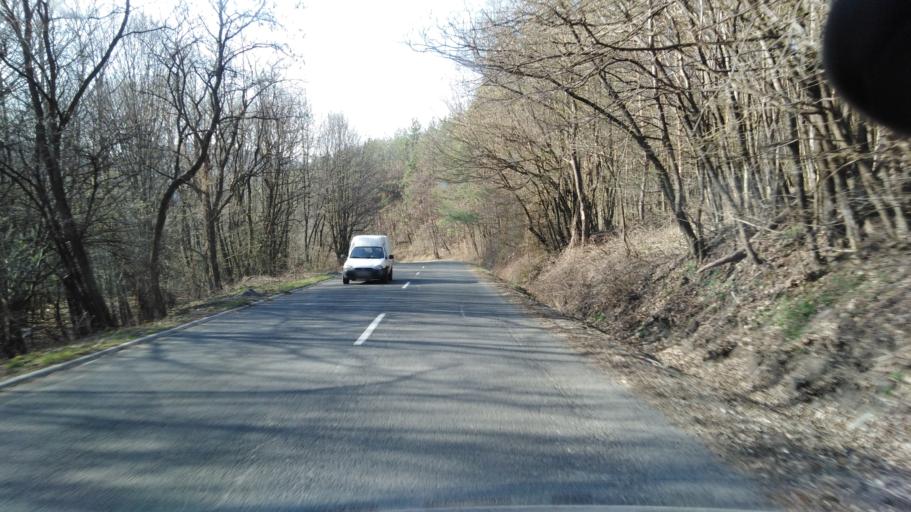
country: HU
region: Nograd
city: Somoskoujfalu
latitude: 48.1586
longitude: 19.8500
